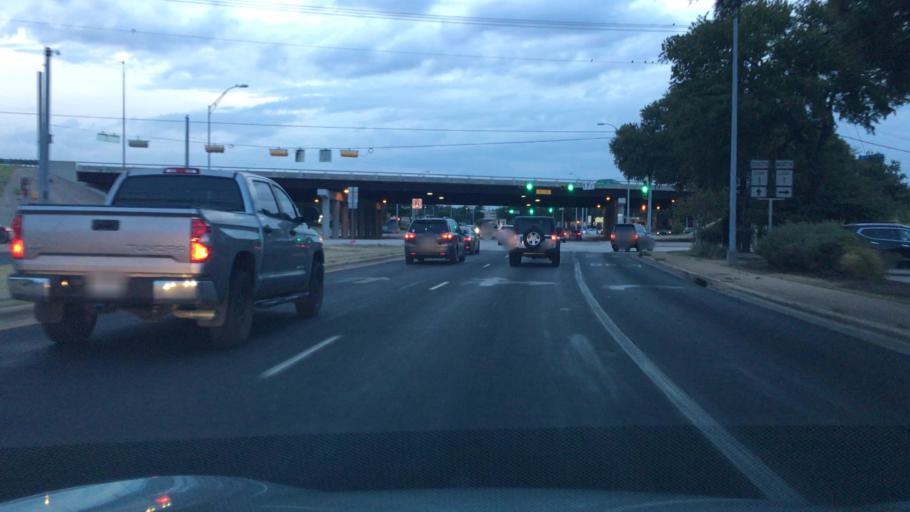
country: US
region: Texas
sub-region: Travis County
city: Shady Hollow
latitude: 30.2193
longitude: -97.8359
